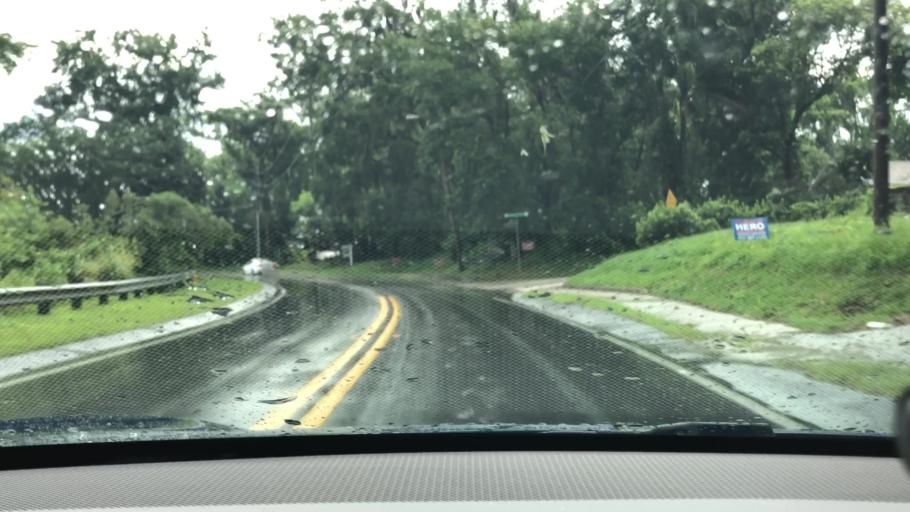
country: US
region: Florida
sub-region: Orange County
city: Edgewood
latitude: 28.4942
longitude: -81.3653
